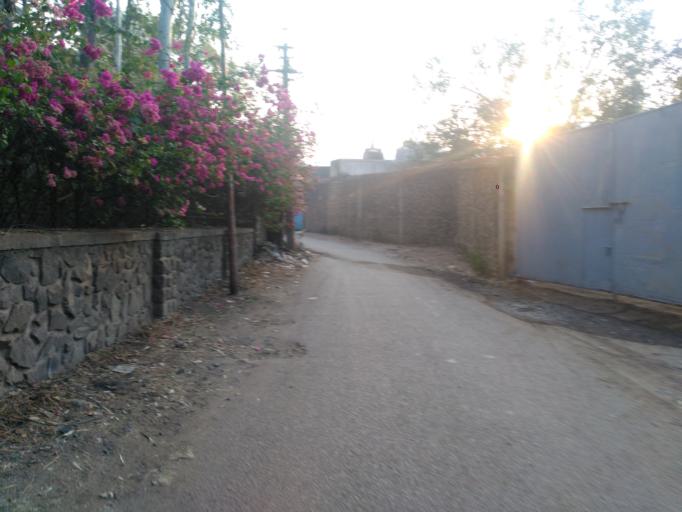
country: IN
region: Maharashtra
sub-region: Pune Division
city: Pune
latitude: 18.4454
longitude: 73.8959
